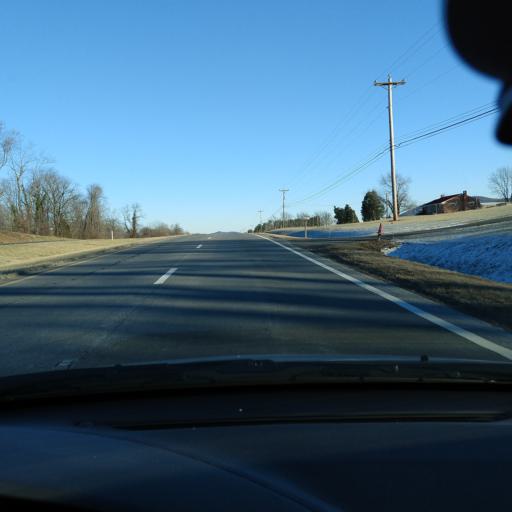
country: US
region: Virginia
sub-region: Botetourt County
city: Blue Ridge
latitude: 37.3597
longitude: -79.6773
